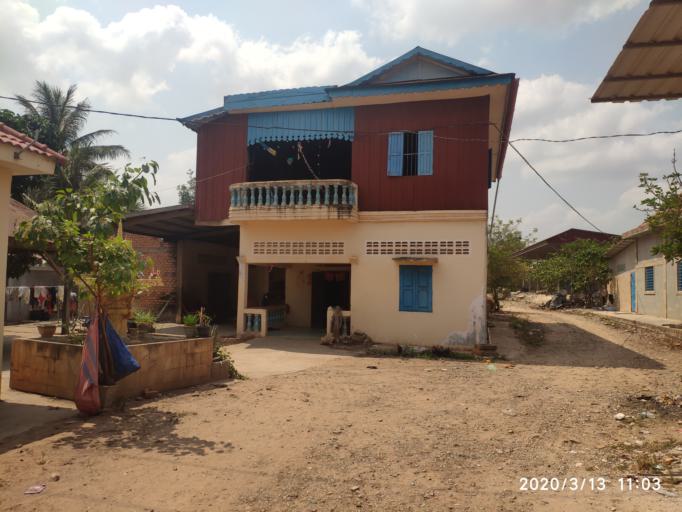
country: KH
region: Banteay Meanchey
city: Sisophon
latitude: 13.6263
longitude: 103.1637
